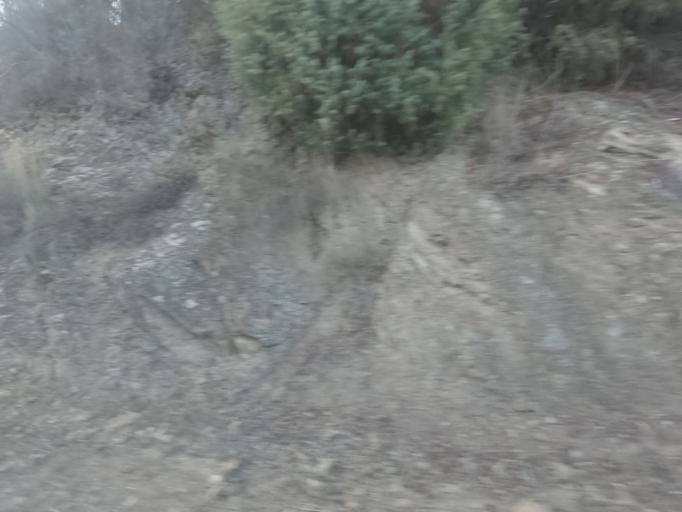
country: PT
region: Viseu
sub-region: Armamar
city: Armamar
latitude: 41.1610
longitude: -7.6815
